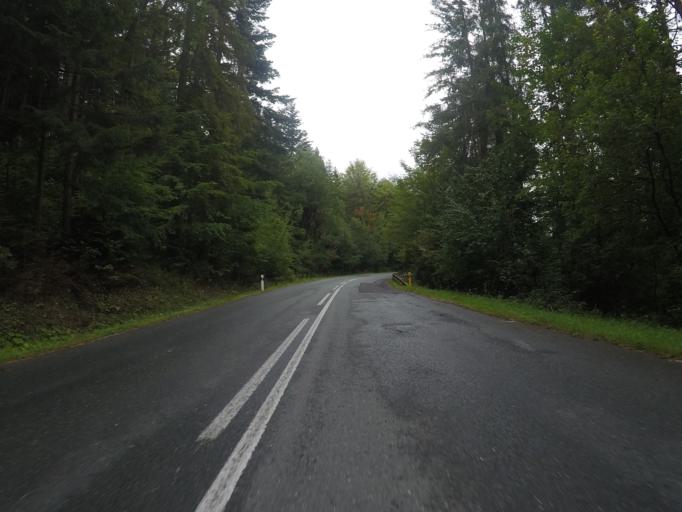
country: SK
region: Kosicky
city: Spisska Nova Ves
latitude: 48.8839
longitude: 20.5369
